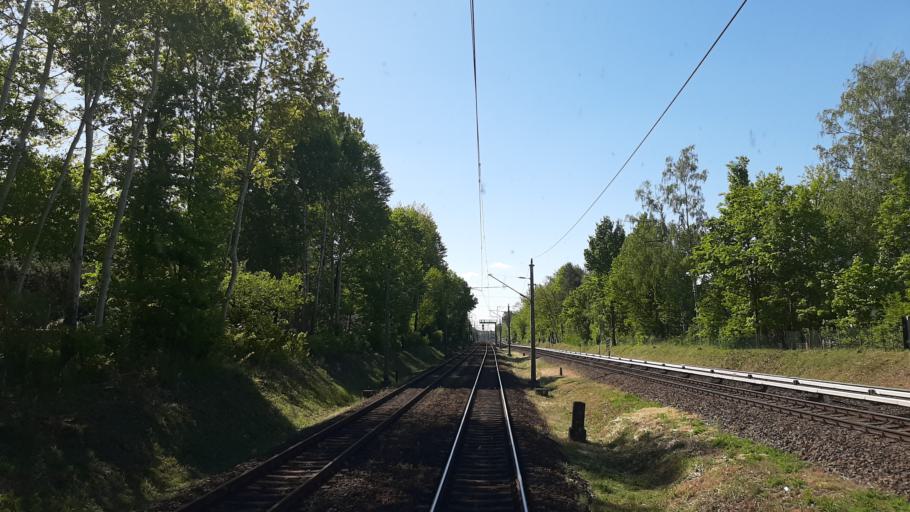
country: DE
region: Brandenburg
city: Birkenwerder
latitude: 52.7064
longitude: 13.2810
